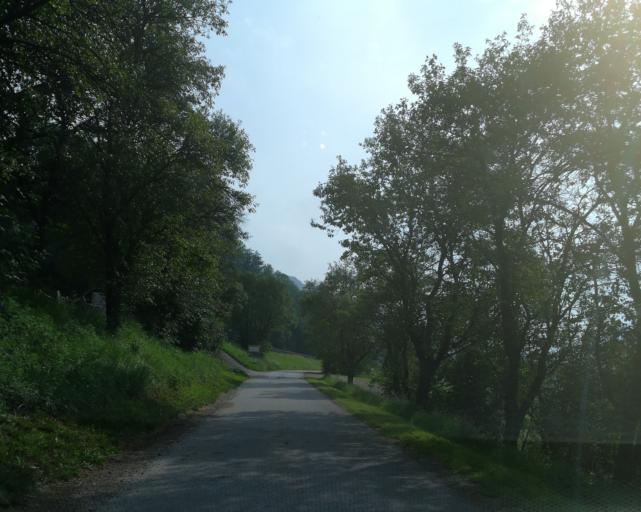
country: AT
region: Styria
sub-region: Politischer Bezirk Murtal
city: Sankt Georgen ob Judenburg
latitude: 47.2157
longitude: 14.4712
